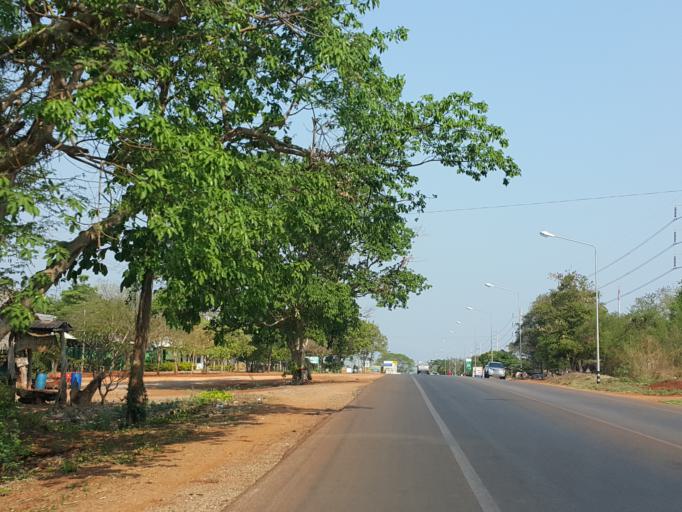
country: TH
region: Kanchanaburi
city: Sai Yok
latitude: 14.1261
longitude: 99.1711
